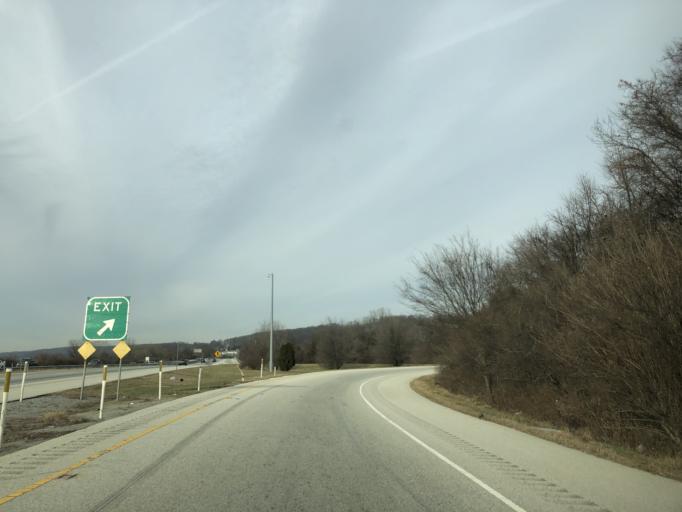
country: US
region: Pennsylvania
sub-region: Chester County
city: Downingtown
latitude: 40.0179
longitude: -75.6682
